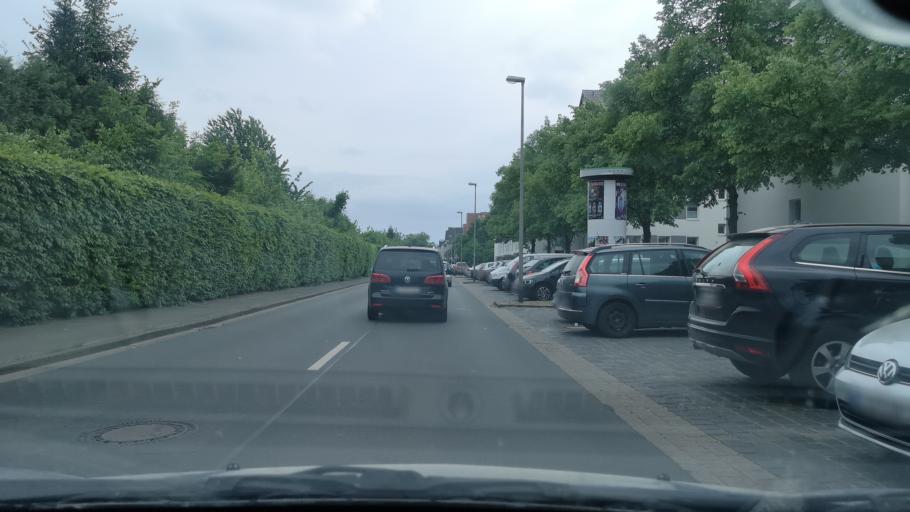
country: DE
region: Lower Saxony
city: Hannover
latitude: 52.4072
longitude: 9.6952
